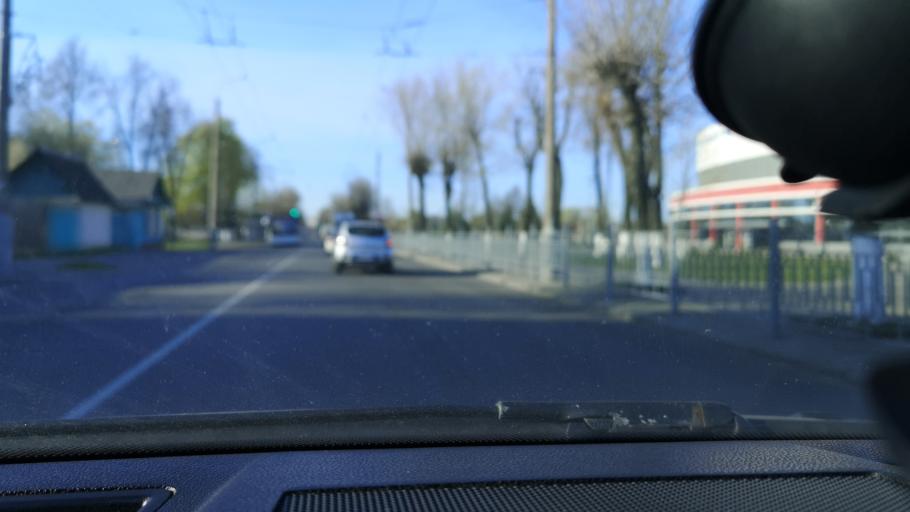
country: BY
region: Gomel
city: Gomel
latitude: 52.4324
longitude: 30.9757
